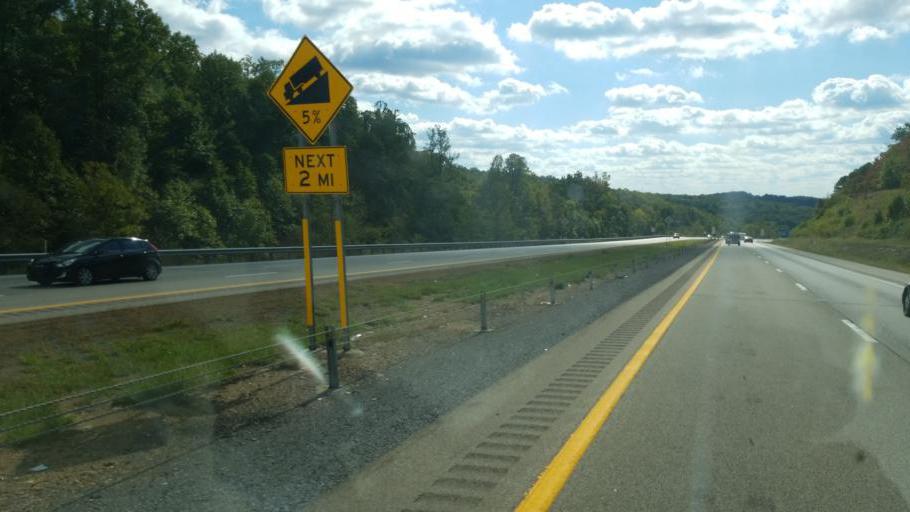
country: US
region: West Virginia
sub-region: Monongalia County
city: Cheat Lake
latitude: 39.6605
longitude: -79.8228
